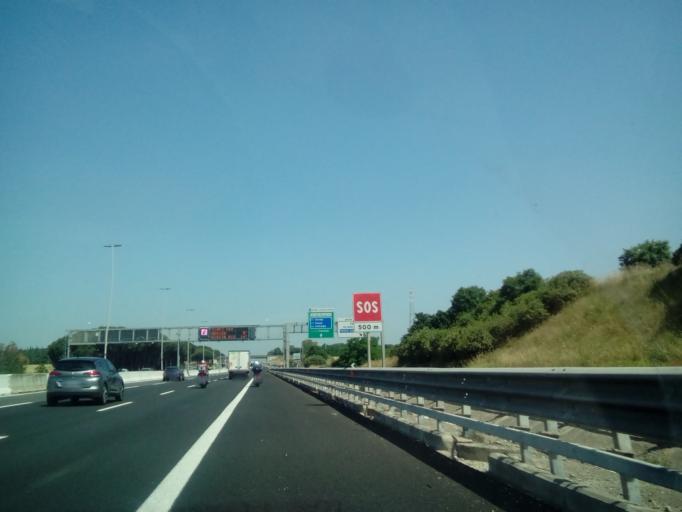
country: IT
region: Latium
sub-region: Citta metropolitana di Roma Capitale
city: La Massimina-Casal Lumbroso
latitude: 41.8460
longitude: 12.3816
